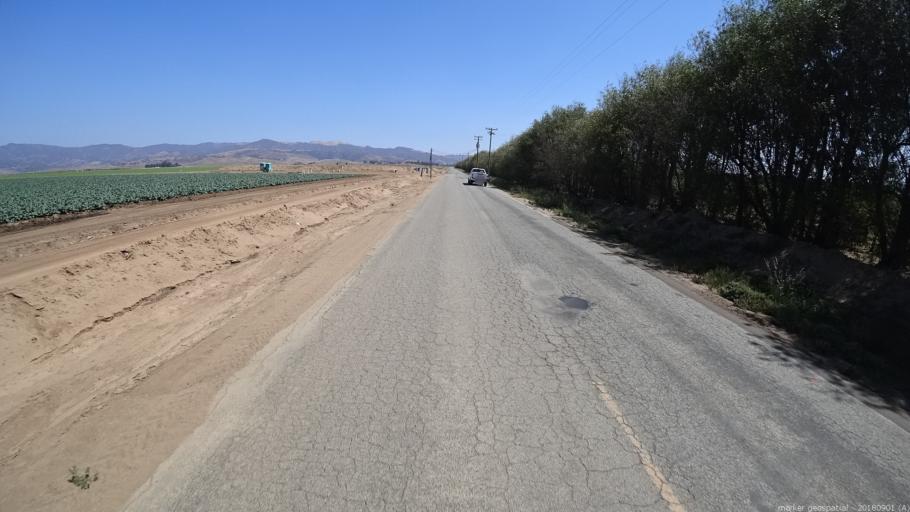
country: US
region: California
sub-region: Monterey County
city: Chualar
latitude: 36.5796
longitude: -121.4861
